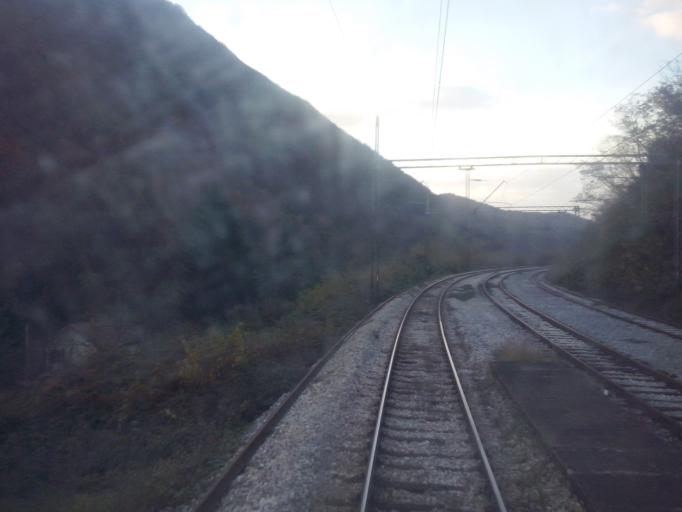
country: RS
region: Central Serbia
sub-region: Kolubarski Okrug
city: Valjevo
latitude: 44.1566
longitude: 19.8859
